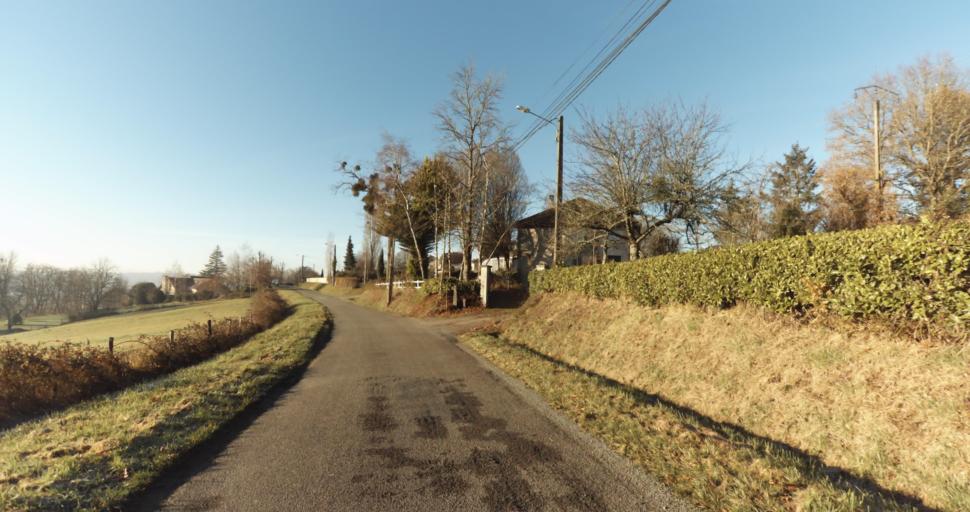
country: FR
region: Limousin
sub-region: Departement de la Haute-Vienne
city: Aixe-sur-Vienne
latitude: 45.8051
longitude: 1.1406
